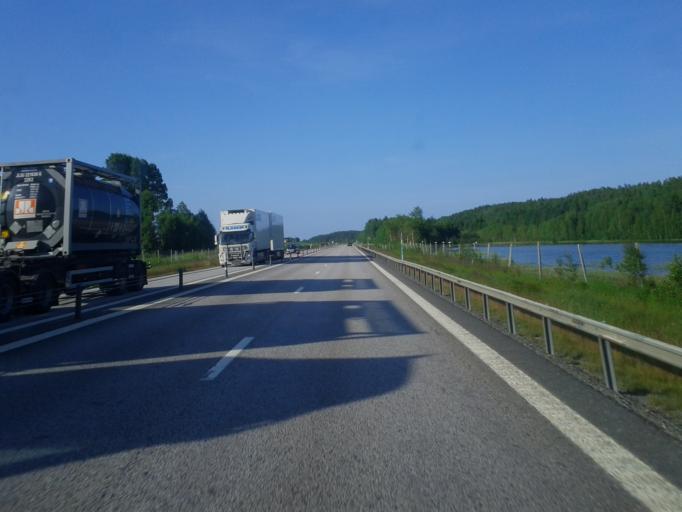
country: SE
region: Vaesterbotten
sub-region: Robertsfors Kommun
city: Robertsfors
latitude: 64.1459
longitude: 20.9005
